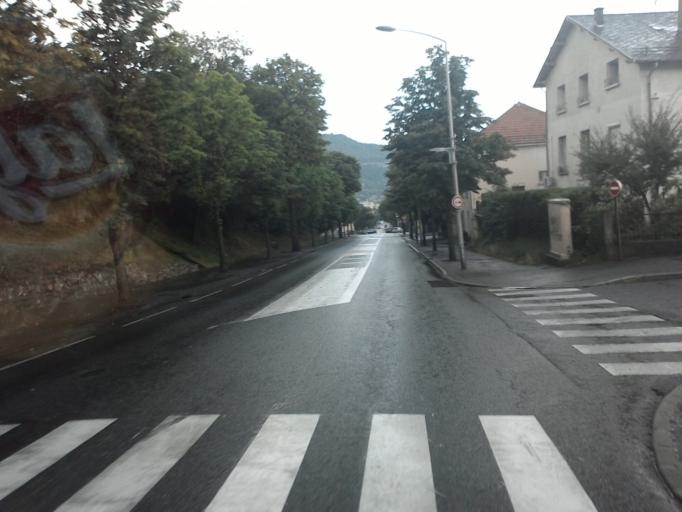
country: FR
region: Provence-Alpes-Cote d'Azur
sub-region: Departement des Hautes-Alpes
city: Gap
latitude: 44.5687
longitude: 6.0833
